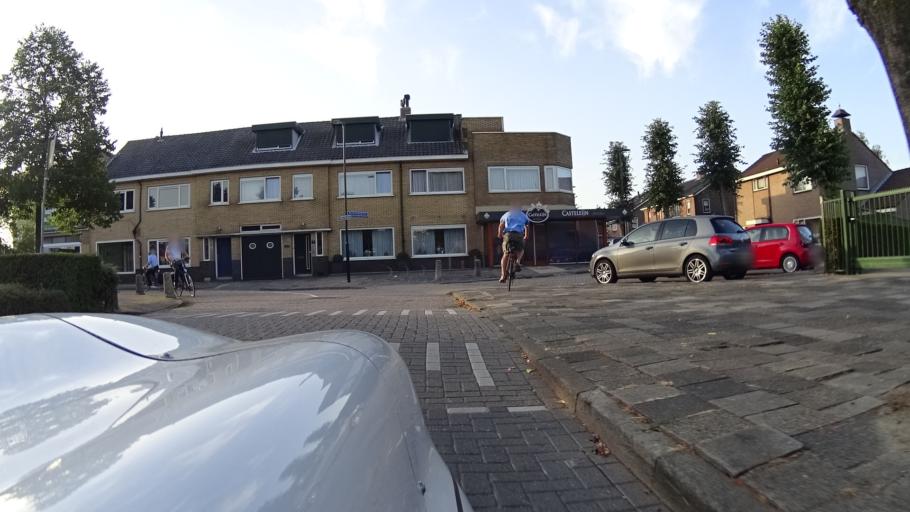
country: NL
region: South Holland
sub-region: Gemeente Capelle aan den IJssel
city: Capelle aan den IJssel
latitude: 51.9137
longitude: 4.5847
